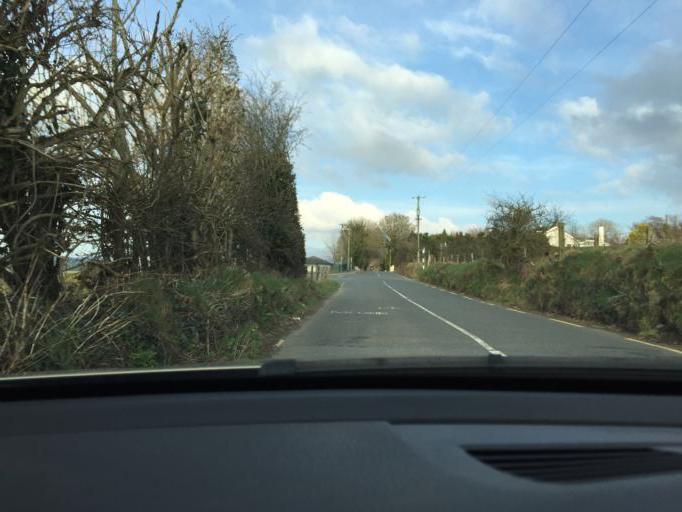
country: IE
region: Leinster
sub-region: Wicklow
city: Blessington
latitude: 53.1689
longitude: -6.5195
